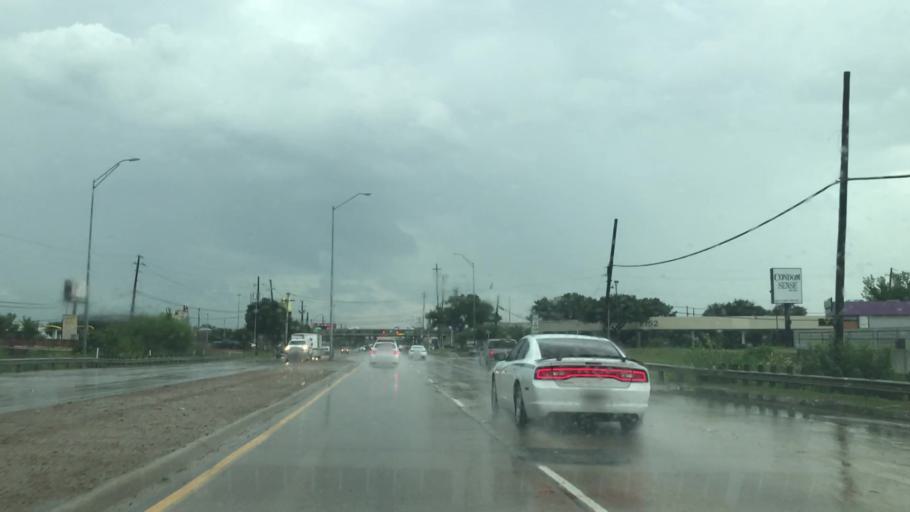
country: US
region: Texas
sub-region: Dallas County
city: Farmers Branch
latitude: 32.8656
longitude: -96.9034
